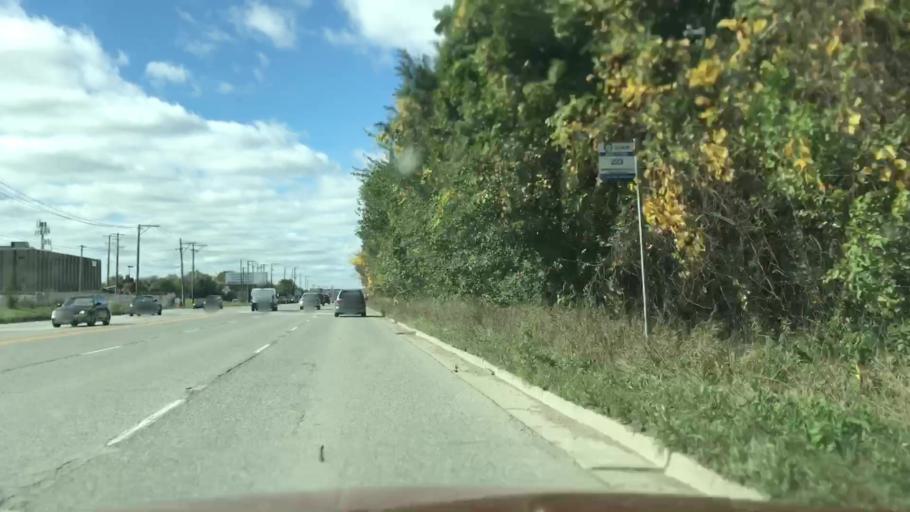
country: US
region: Illinois
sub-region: Cook County
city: Elk Grove Village
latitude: 42.0083
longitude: -87.9289
